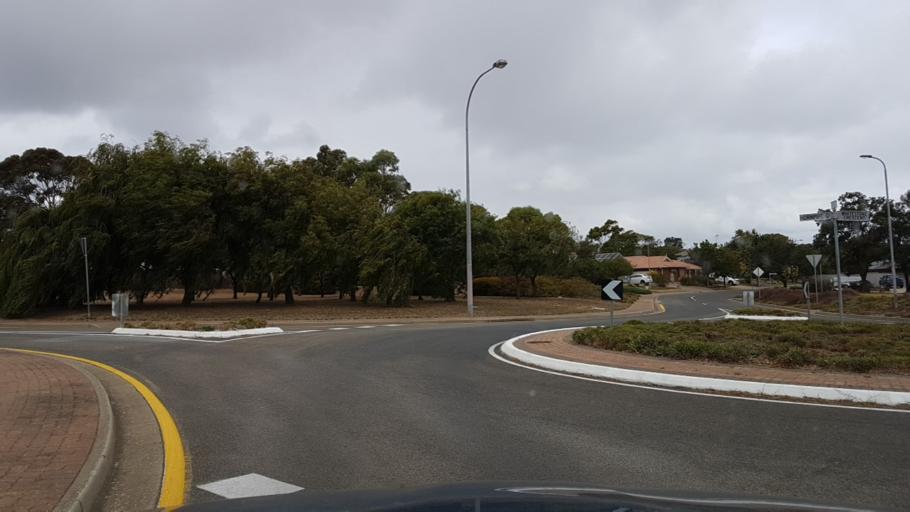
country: AU
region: South Australia
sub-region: Onkaparinga
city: Moana
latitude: -35.1965
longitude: 138.4896
